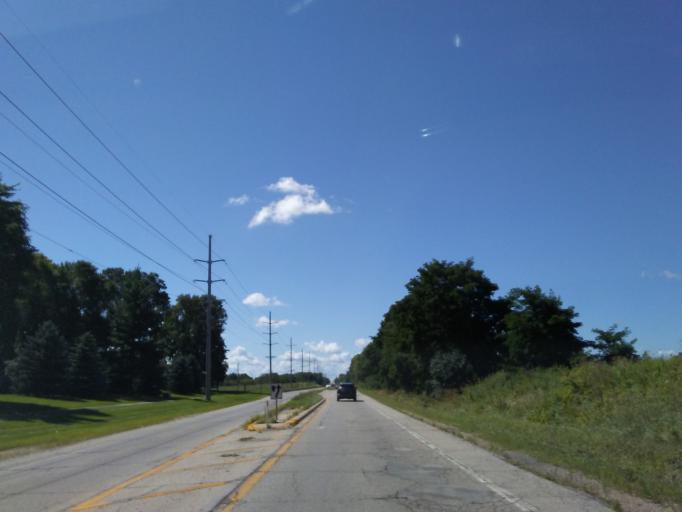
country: US
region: Wisconsin
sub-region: Dane County
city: Verona
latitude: 43.0265
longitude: -89.5334
